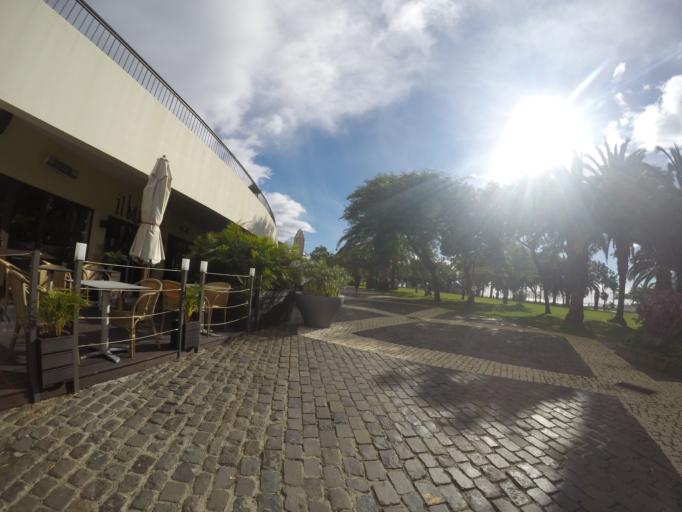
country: PT
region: Madeira
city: Camara de Lobos
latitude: 32.6367
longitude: -16.9336
